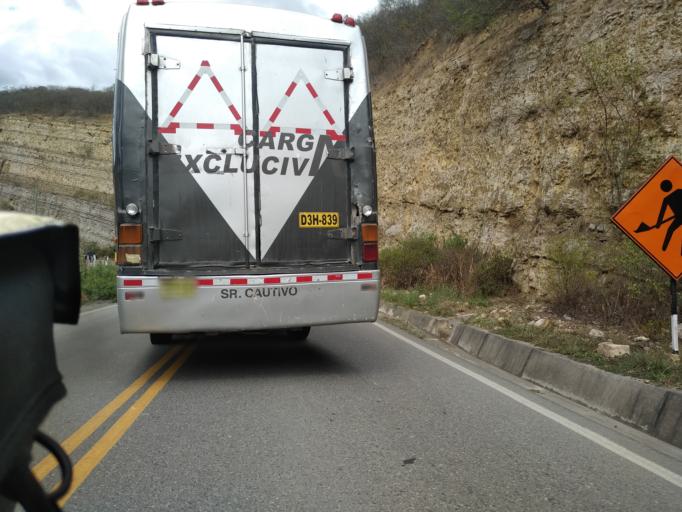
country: PE
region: Amazonas
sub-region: Utcubamba
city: Jamalca
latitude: -5.8468
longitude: -78.2382
